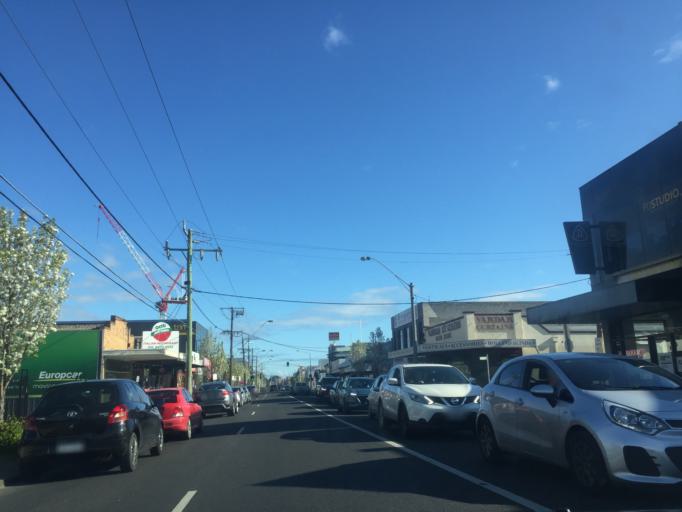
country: AU
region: Victoria
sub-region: Darebin
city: Reservoir
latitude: -37.7322
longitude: 145.0050
